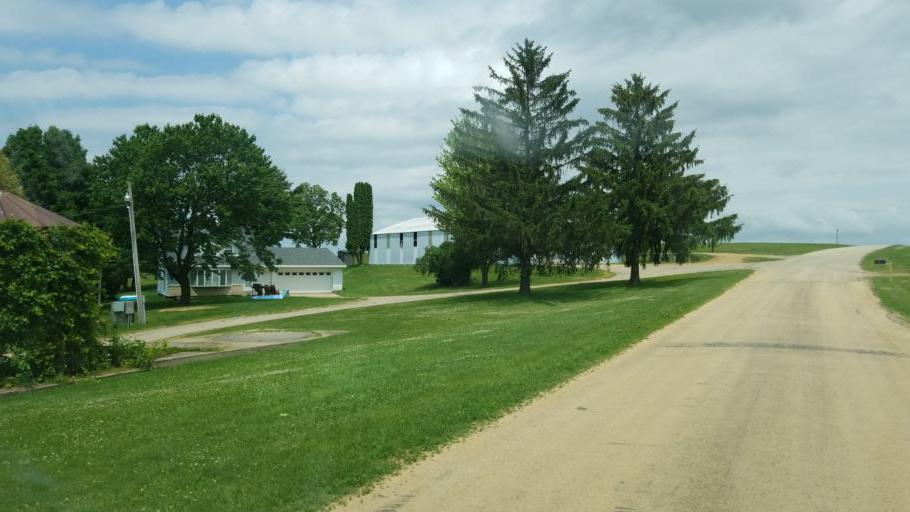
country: US
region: Wisconsin
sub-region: Monroe County
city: Cashton
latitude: 43.7045
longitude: -90.6230
